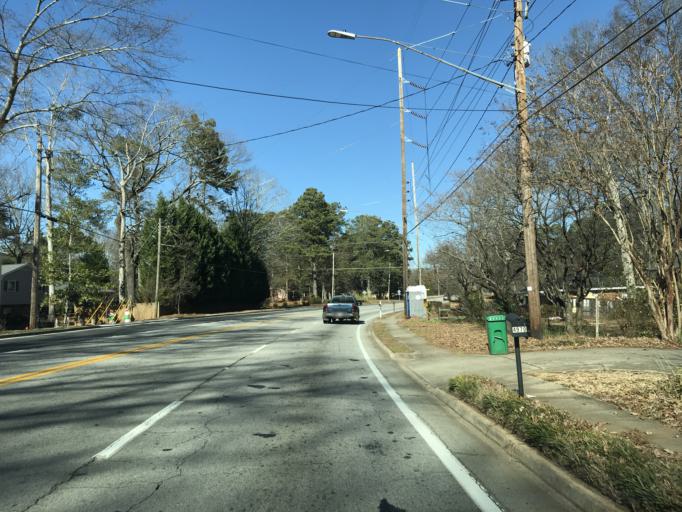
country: US
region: Georgia
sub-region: DeKalb County
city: Tucker
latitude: 33.8600
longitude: -84.2192
